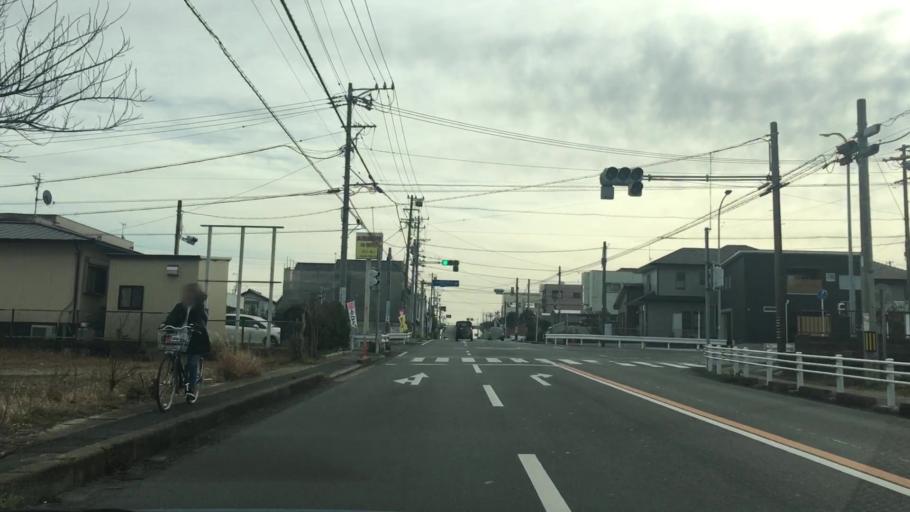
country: JP
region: Aichi
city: Toyohashi
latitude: 34.7195
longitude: 137.3449
